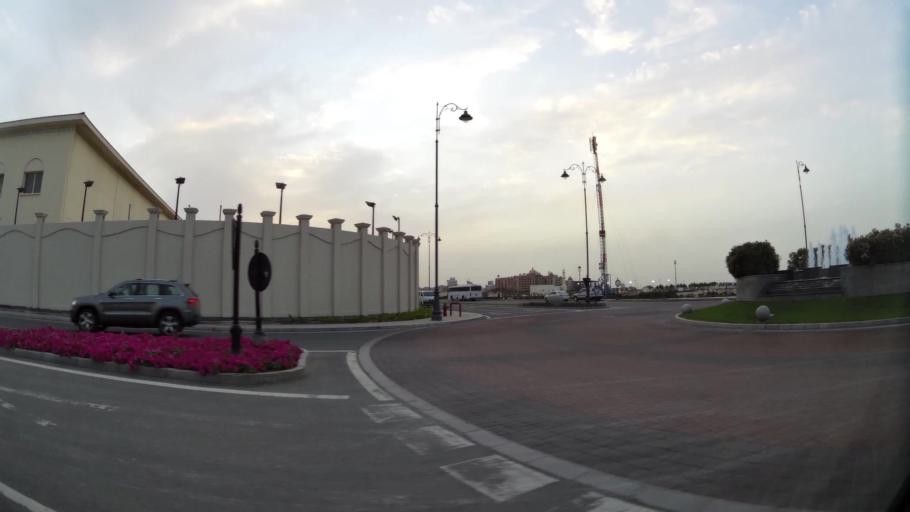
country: QA
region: Baladiyat ad Dawhah
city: Doha
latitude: 25.3726
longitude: 51.5572
